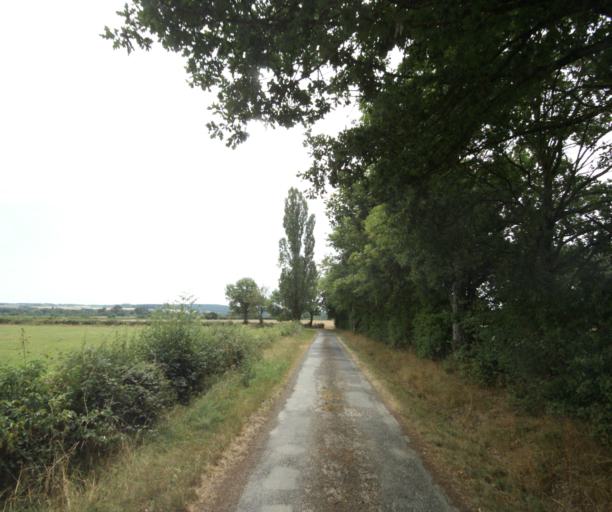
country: FR
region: Bourgogne
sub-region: Departement de Saone-et-Loire
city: Gueugnon
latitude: 46.5767
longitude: 4.0396
